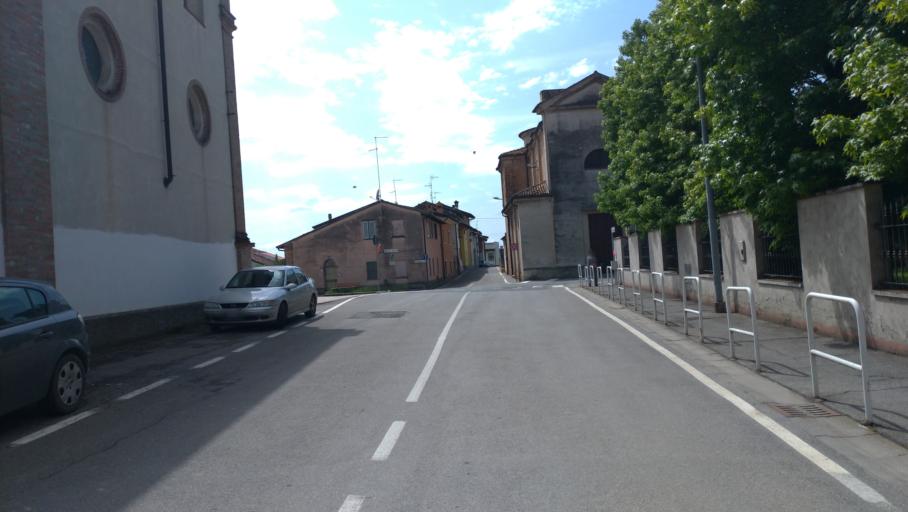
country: IT
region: Lombardy
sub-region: Provincia di Cremona
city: Madignano
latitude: 45.3427
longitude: 9.7263
